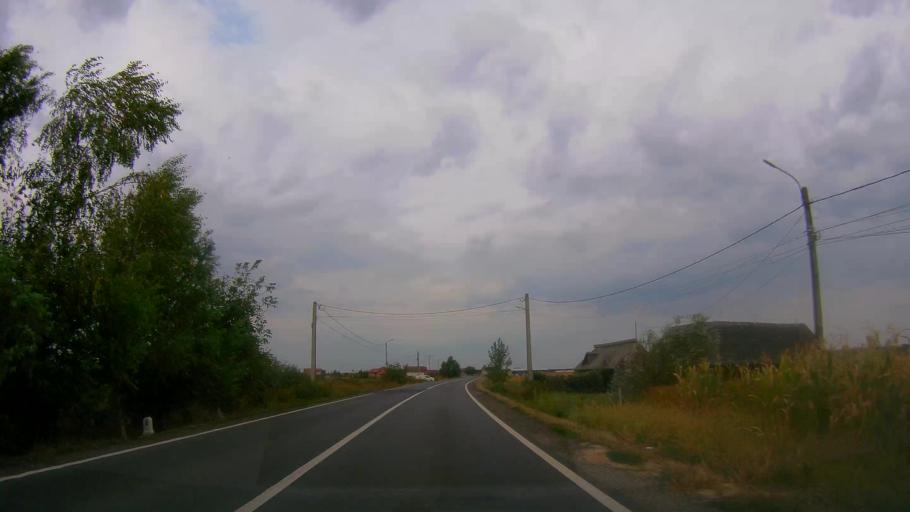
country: RO
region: Satu Mare
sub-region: Comuna Agris
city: Agris
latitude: 47.8711
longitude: 23.0297
